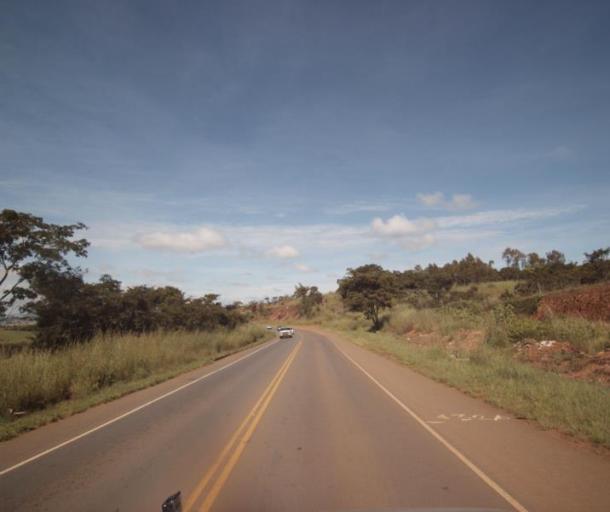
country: BR
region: Goias
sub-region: Anapolis
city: Anapolis
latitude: -16.2289
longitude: -48.9283
